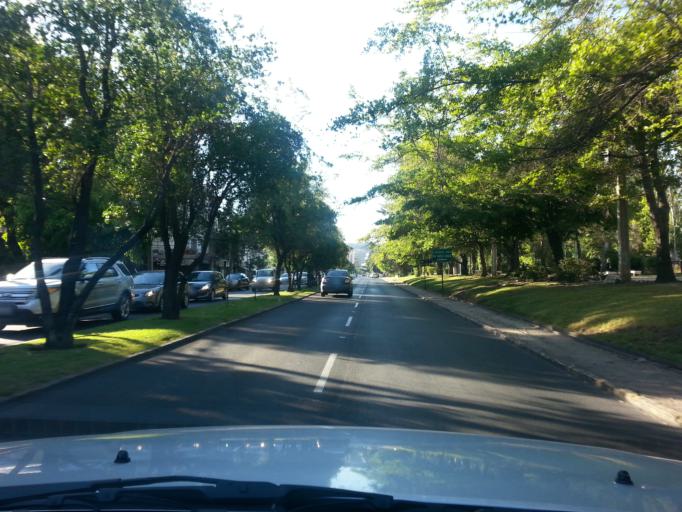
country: CL
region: Santiago Metropolitan
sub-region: Provincia de Santiago
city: Villa Presidente Frei, Nunoa, Santiago, Chile
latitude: -33.4277
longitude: -70.5893
